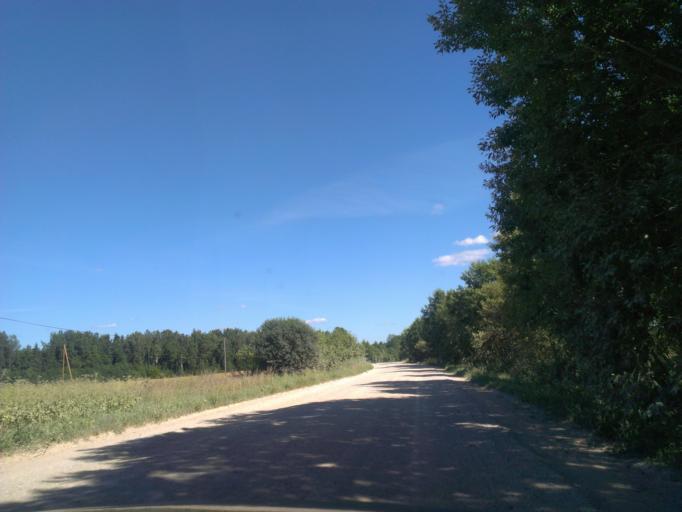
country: LV
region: Malpils
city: Malpils
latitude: 57.0149
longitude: 25.0025
